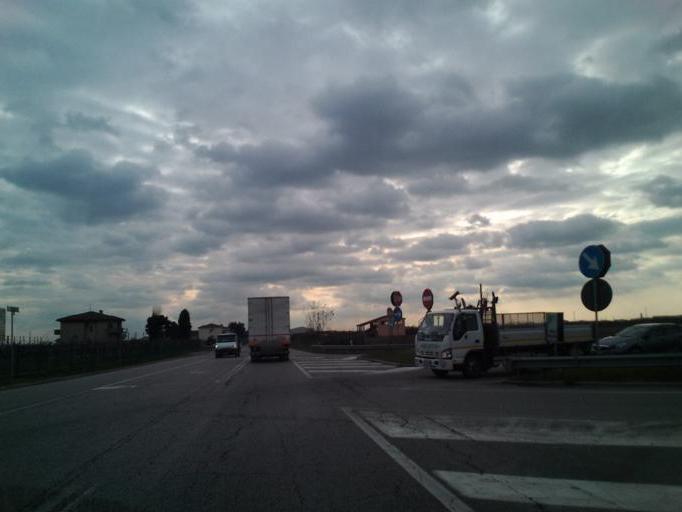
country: IT
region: Veneto
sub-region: Provincia di Verona
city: Beccacivetta-Azzano
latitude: 45.3985
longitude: 10.9439
